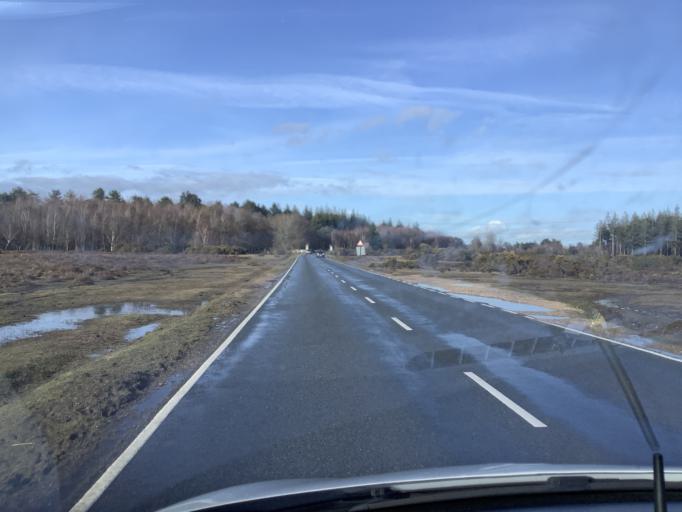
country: GB
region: England
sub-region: Hampshire
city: Hythe
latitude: 50.8456
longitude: -1.4241
